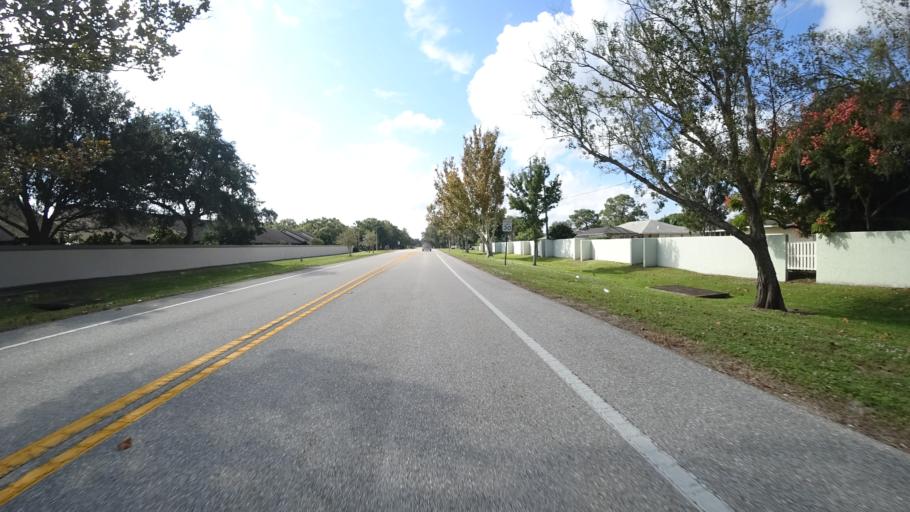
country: US
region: Florida
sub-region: Sarasota County
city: Desoto Lakes
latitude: 27.3942
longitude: -82.4872
